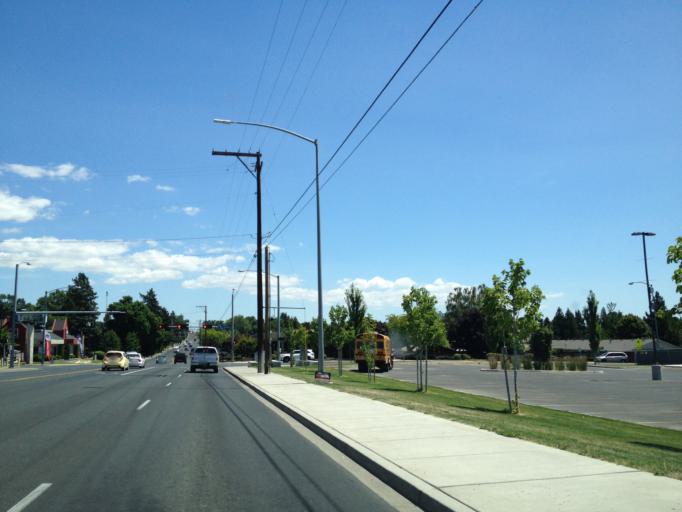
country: US
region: Washington
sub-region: Yakima County
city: West Valley
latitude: 46.5926
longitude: -120.5633
